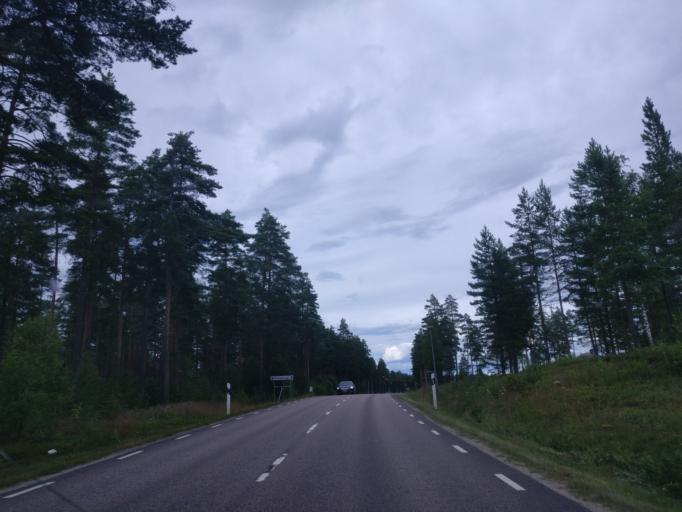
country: SE
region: Vaermland
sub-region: Hagfors Kommun
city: Ekshaerad
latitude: 60.1692
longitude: 13.4810
